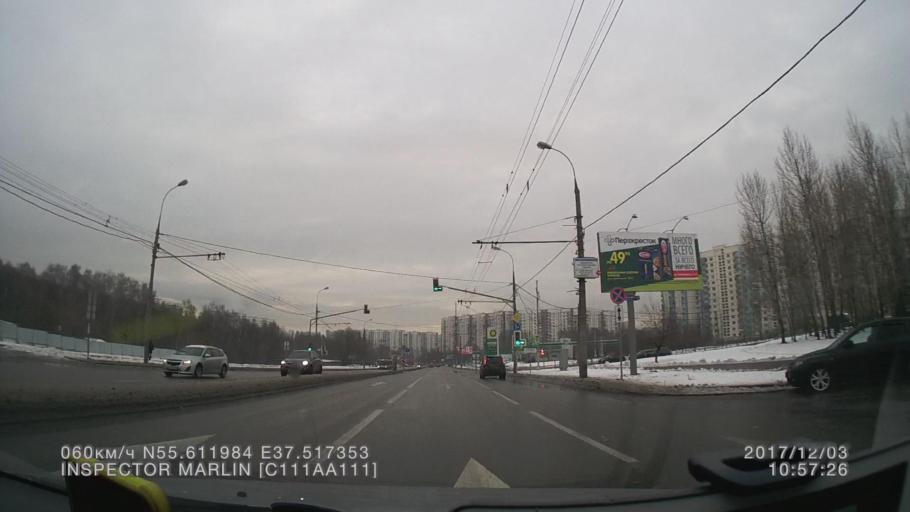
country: RU
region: Moscow
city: Yasenevo
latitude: 55.6119
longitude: 37.5175
